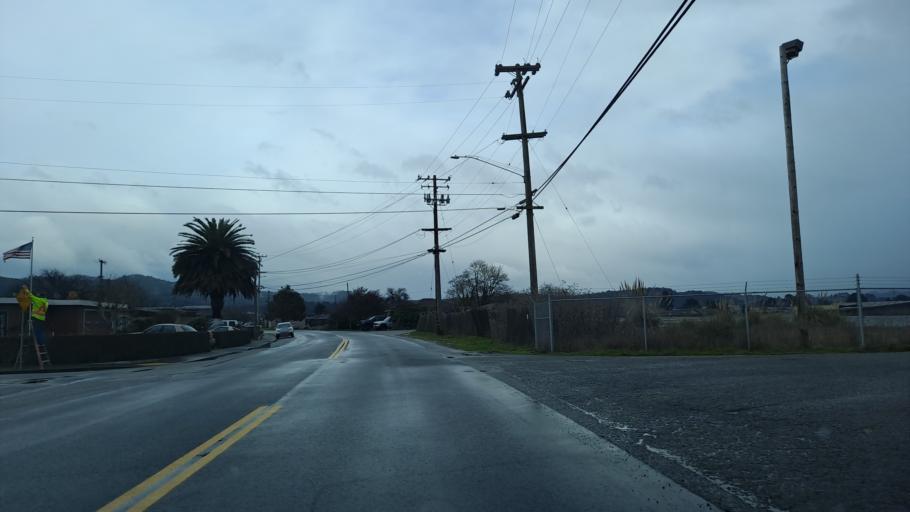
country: US
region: California
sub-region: Humboldt County
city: Fortuna
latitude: 40.5889
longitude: -124.1529
